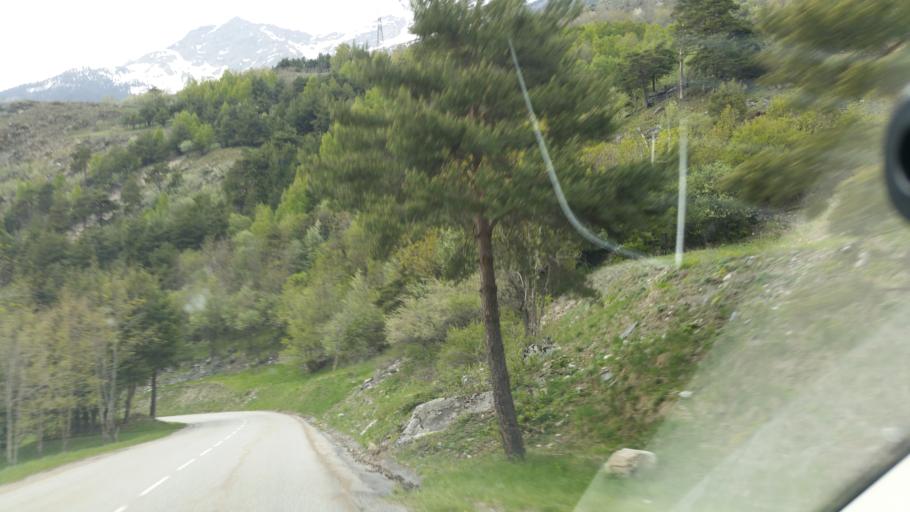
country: FR
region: Rhone-Alpes
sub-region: Departement de la Savoie
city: Modane
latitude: 45.2036
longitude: 6.6076
